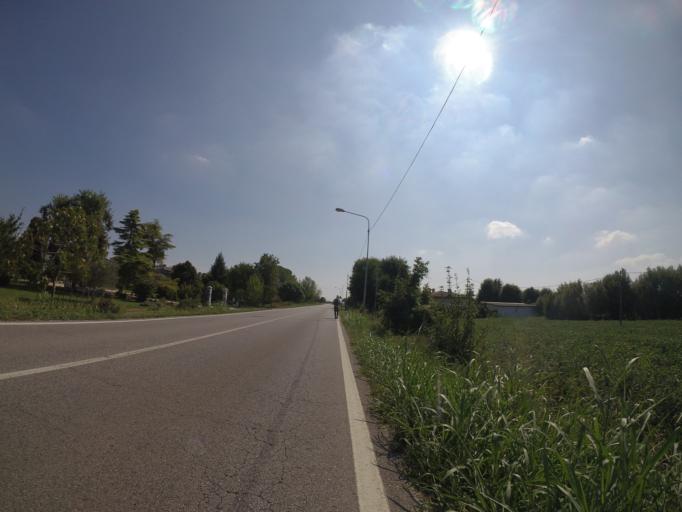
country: IT
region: Friuli Venezia Giulia
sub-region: Provincia di Udine
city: Pocenia
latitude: 45.8250
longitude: 13.1007
